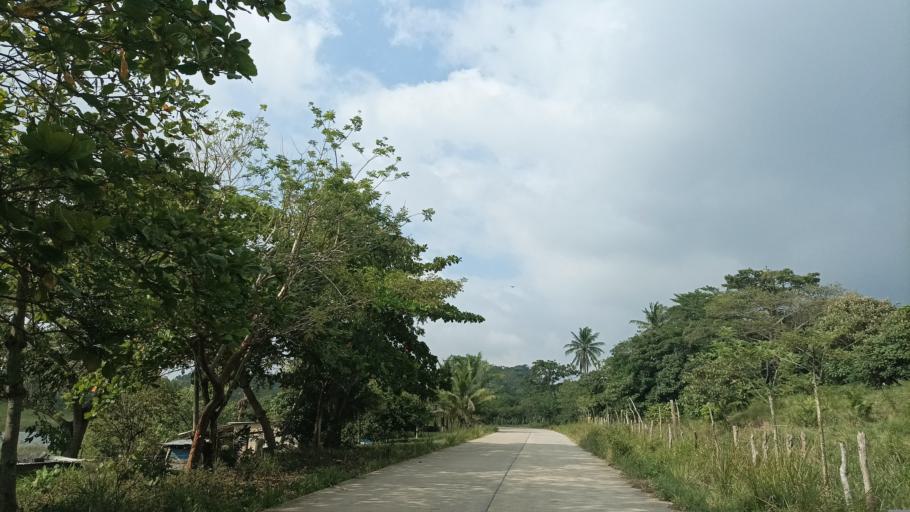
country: MX
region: Veracruz
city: Allende
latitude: 18.0946
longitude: -94.2930
